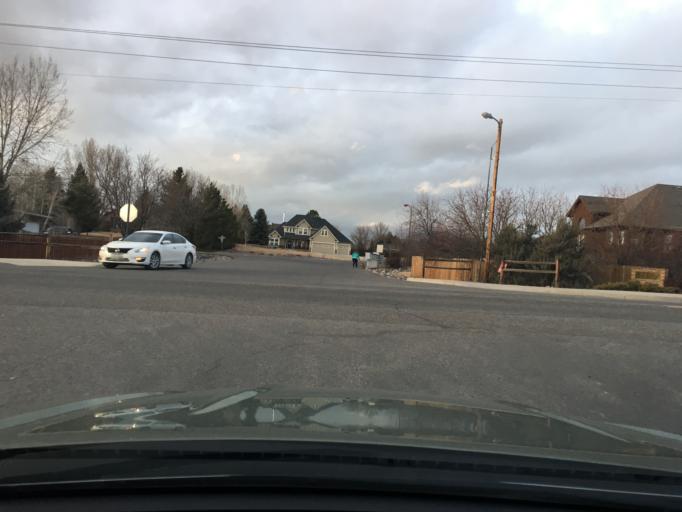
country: US
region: Colorado
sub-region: Montrose County
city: Montrose
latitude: 38.4671
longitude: -107.8406
